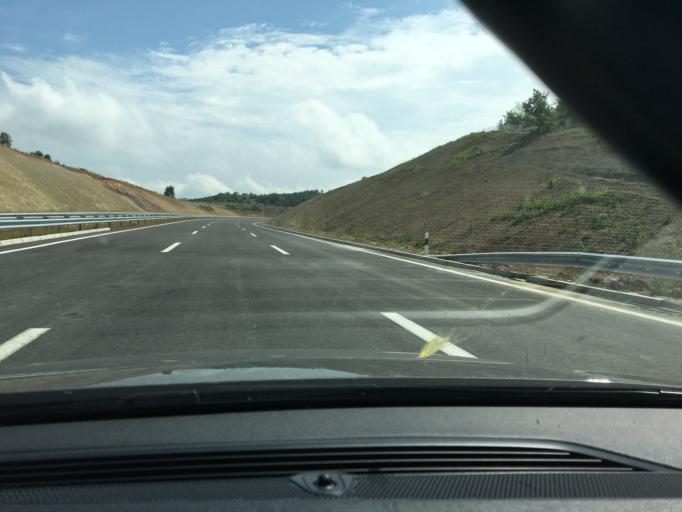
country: MK
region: Petrovec
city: Sredno Konjare
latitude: 41.9455
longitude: 21.7933
